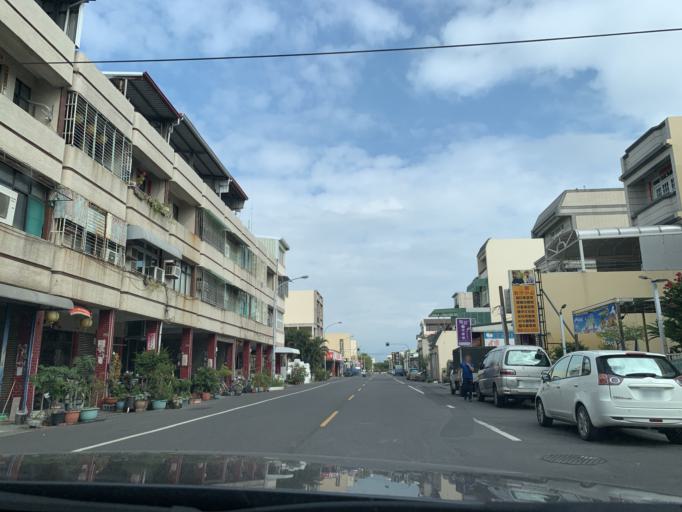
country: TW
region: Taiwan
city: Fengshan
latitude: 22.4670
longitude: 120.4569
